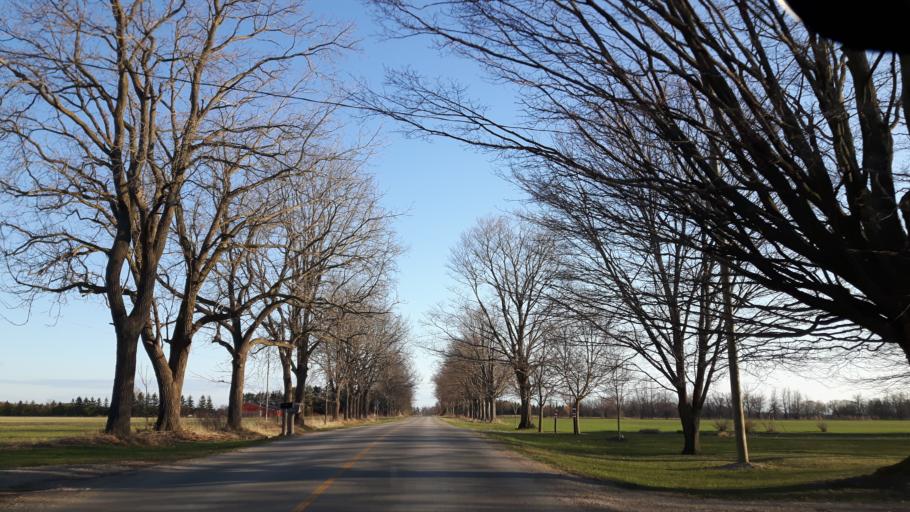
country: CA
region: Ontario
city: Goderich
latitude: 43.6557
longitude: -81.6847
